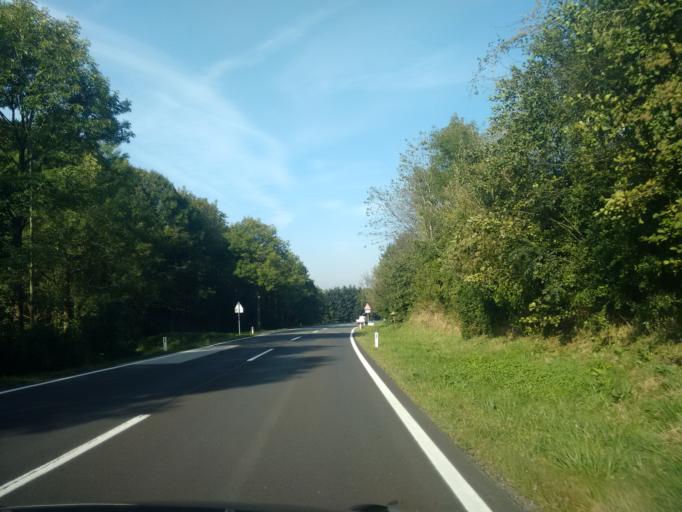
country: AT
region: Upper Austria
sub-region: Politischer Bezirk Grieskirchen
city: Grieskirchen
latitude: 48.2882
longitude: 13.6681
